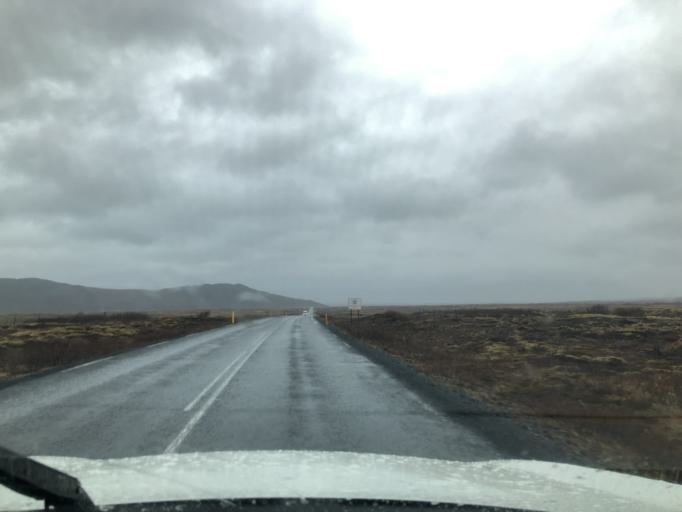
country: IS
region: South
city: Hveragerdi
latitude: 64.2050
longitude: -21.0392
